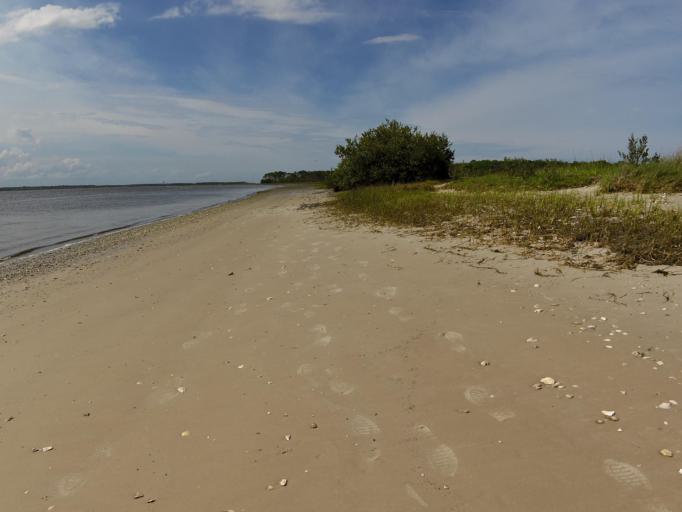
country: US
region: Florida
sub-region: Saint Johns County
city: Villano Beach
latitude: 30.0168
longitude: -81.3460
